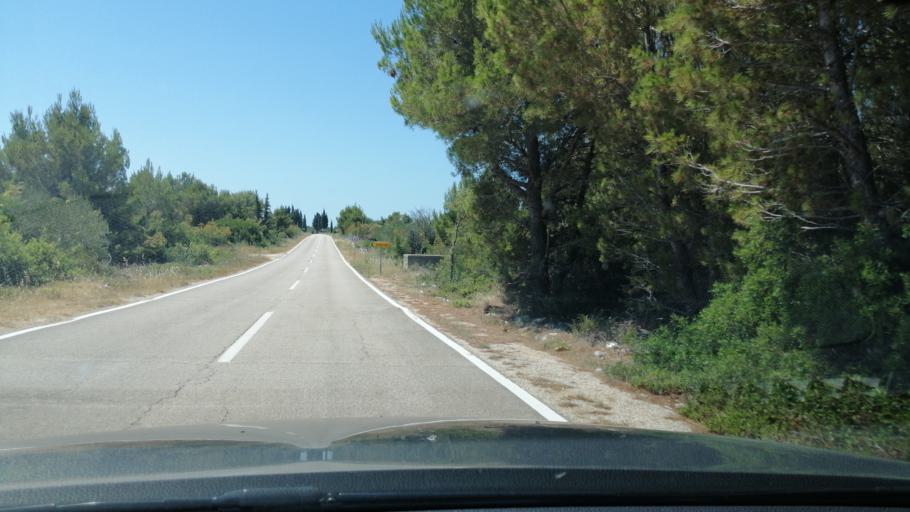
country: HR
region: Sibensko-Kniniska
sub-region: Grad Sibenik
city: Pirovac
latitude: 43.8317
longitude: 15.6829
